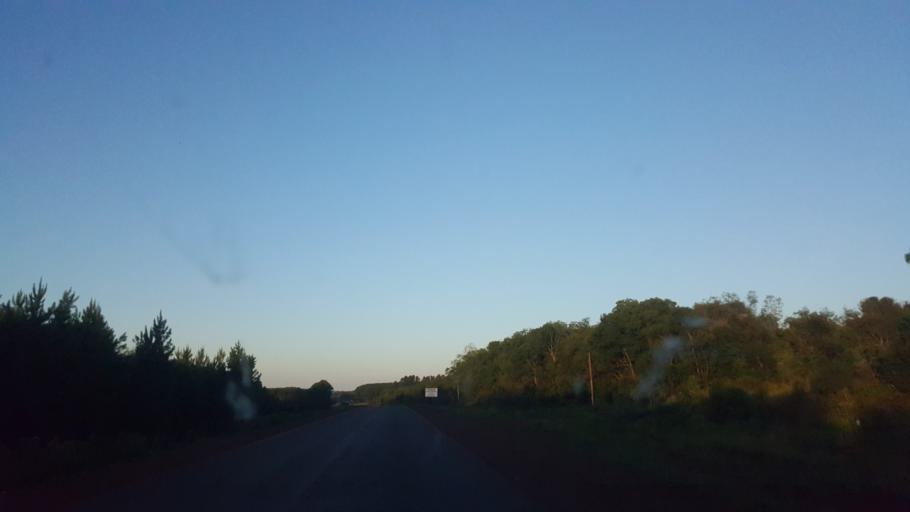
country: AR
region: Corrientes
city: Santo Tome
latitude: -28.4313
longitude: -55.9961
